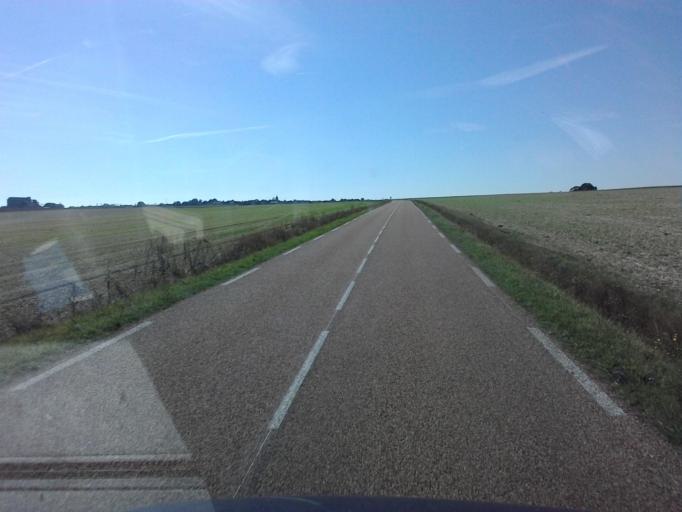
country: FR
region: Bourgogne
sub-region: Departement de l'Yonne
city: Joux-la-Ville
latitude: 47.6850
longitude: 3.8878
